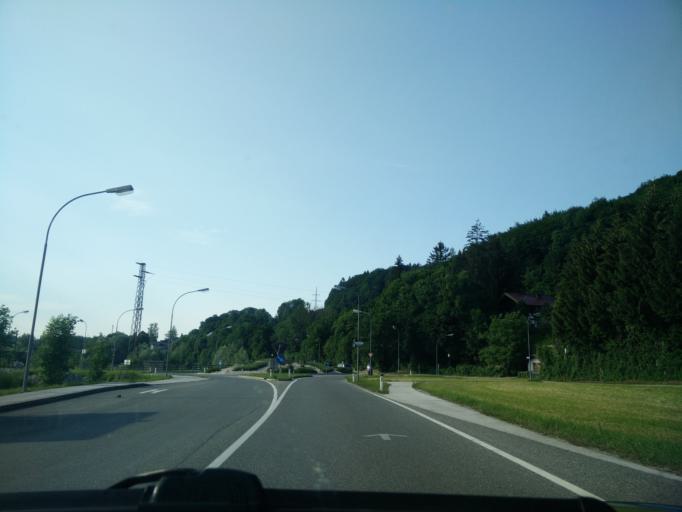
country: AT
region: Salzburg
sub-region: Politischer Bezirk Salzburg-Umgebung
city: Elsbethen
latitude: 47.7362
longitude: 13.0892
